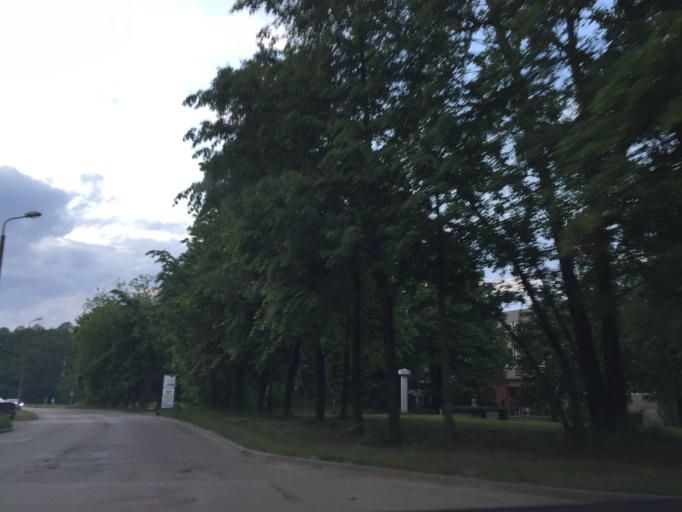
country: LV
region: Riga
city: Riga
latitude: 56.9729
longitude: 24.0635
